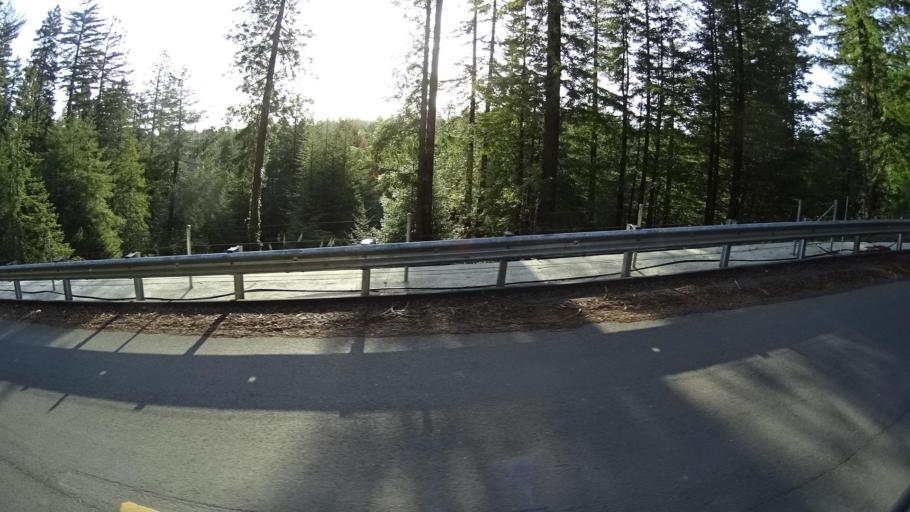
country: US
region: California
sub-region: Humboldt County
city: Myrtletown
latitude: 40.7726
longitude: -124.1144
